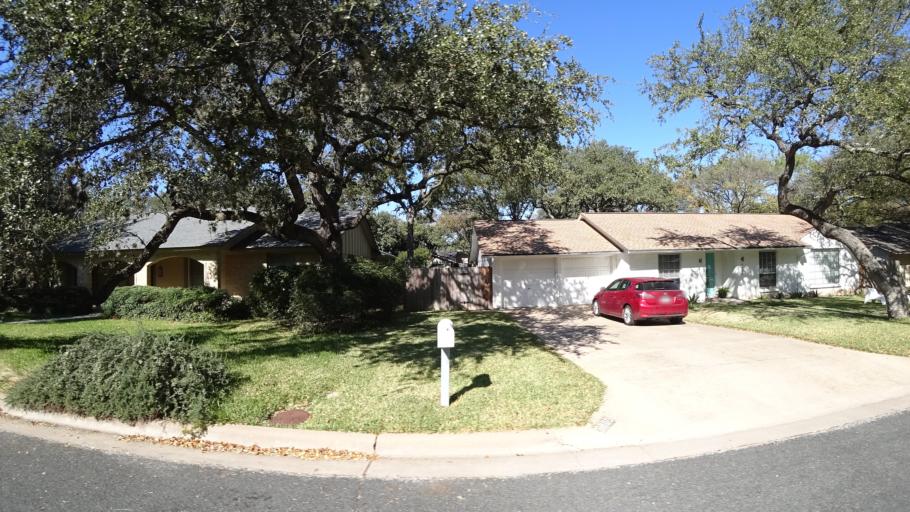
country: US
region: Texas
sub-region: Williamson County
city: Jollyville
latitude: 30.3817
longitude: -97.7491
